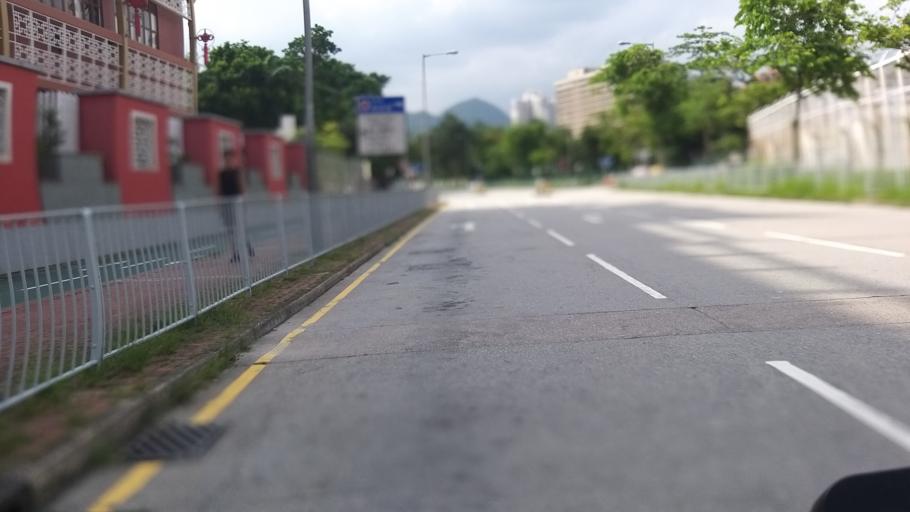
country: HK
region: Tuen Mun
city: Tuen Mun
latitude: 22.4059
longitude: 113.9749
